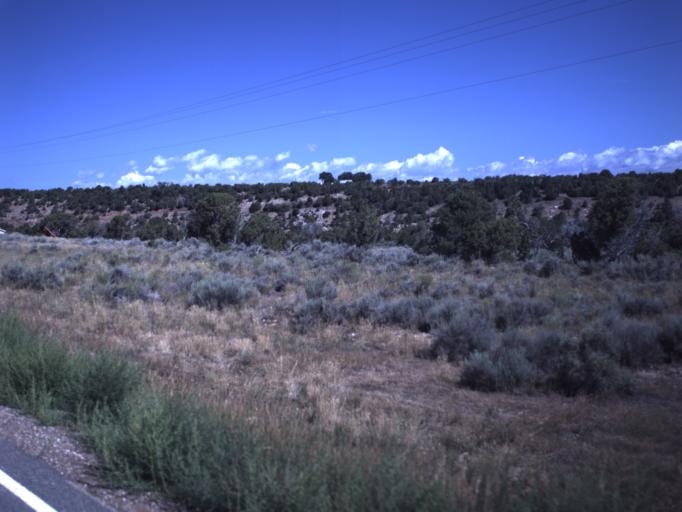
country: US
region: Utah
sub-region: Duchesne County
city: Duchesne
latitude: 40.3189
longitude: -110.3944
